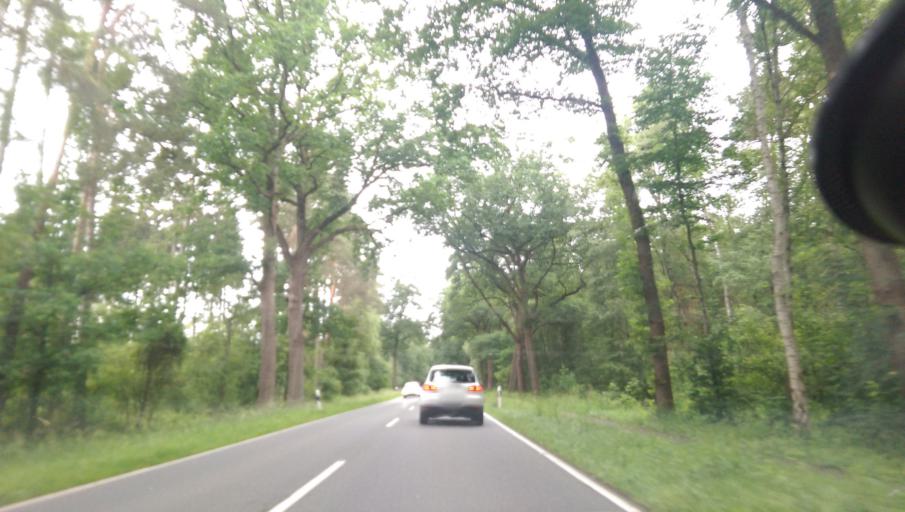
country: DE
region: Lower Saxony
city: Rotenburg
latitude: 53.0829
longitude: 9.4244
